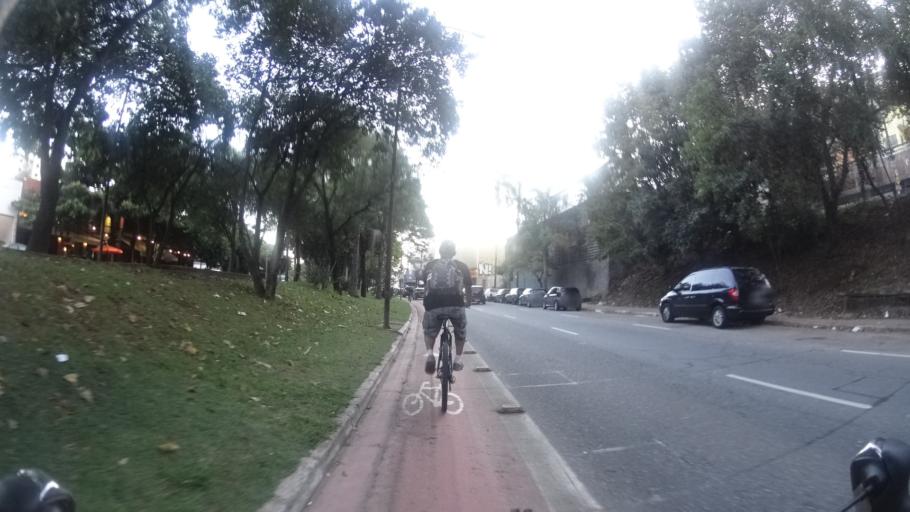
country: BR
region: Sao Paulo
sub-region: Sao Paulo
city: Sao Paulo
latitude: -23.4835
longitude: -46.6363
